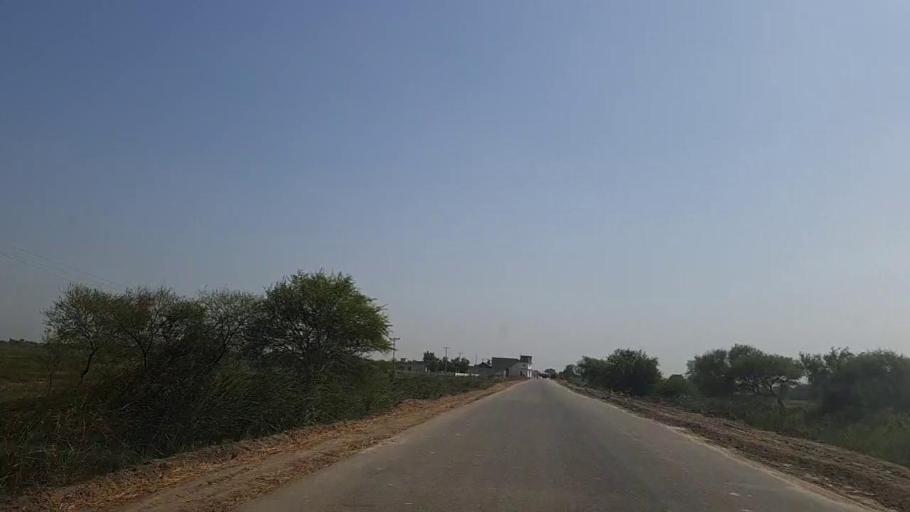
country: PK
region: Sindh
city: Daro Mehar
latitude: 24.7801
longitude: 68.1993
